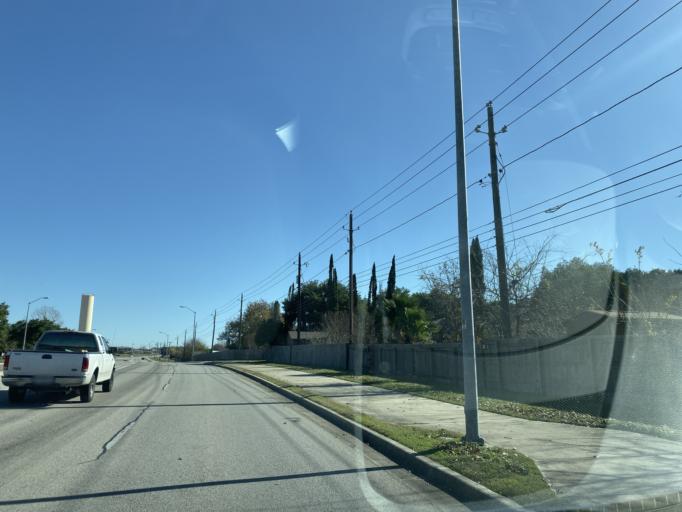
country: US
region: Texas
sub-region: Travis County
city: Windemere
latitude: 30.4713
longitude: -97.6497
